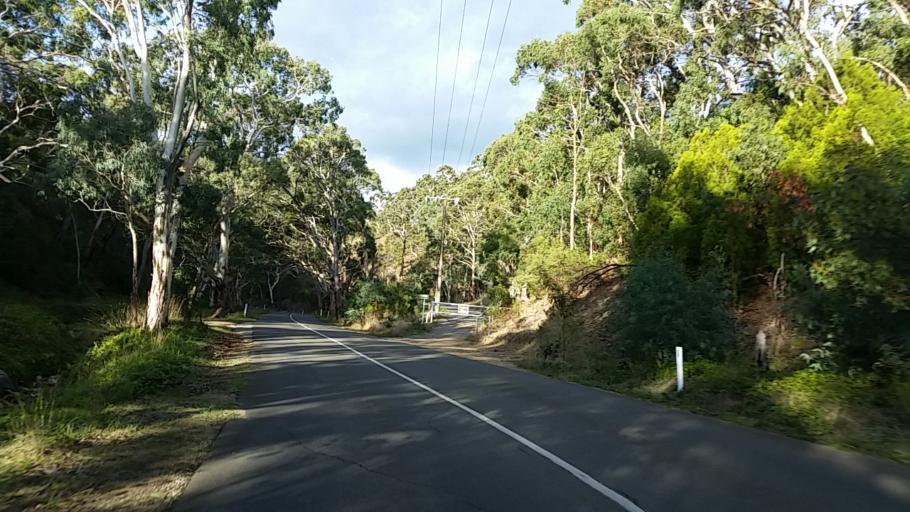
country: AU
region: South Australia
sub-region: Adelaide Hills
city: Adelaide Hills
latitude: -34.8897
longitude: 138.7213
